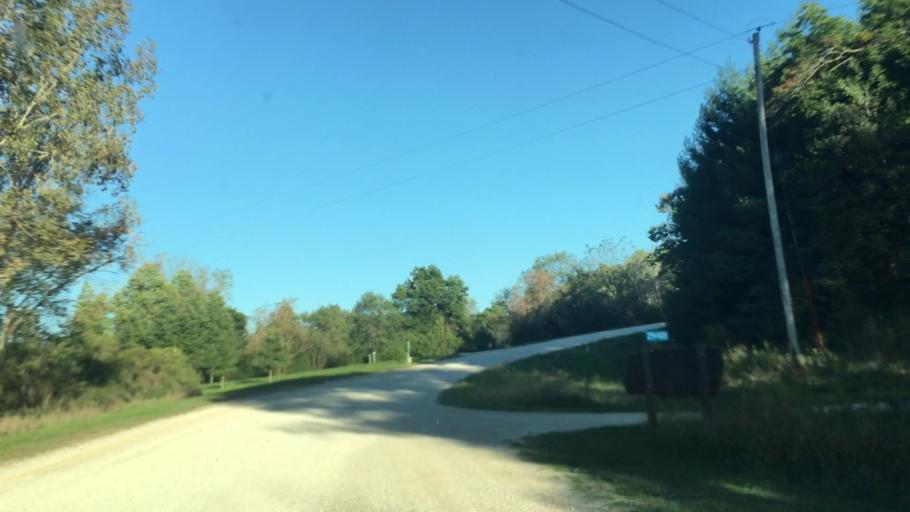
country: US
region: Minnesota
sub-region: Fillmore County
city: Preston
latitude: 43.7827
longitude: -92.0313
